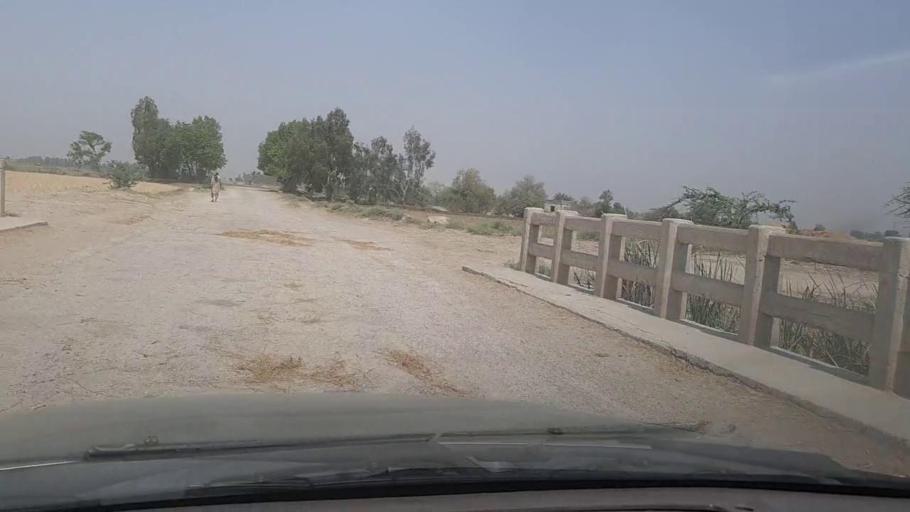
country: PK
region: Sindh
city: Madeji
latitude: 27.8300
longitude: 68.3900
